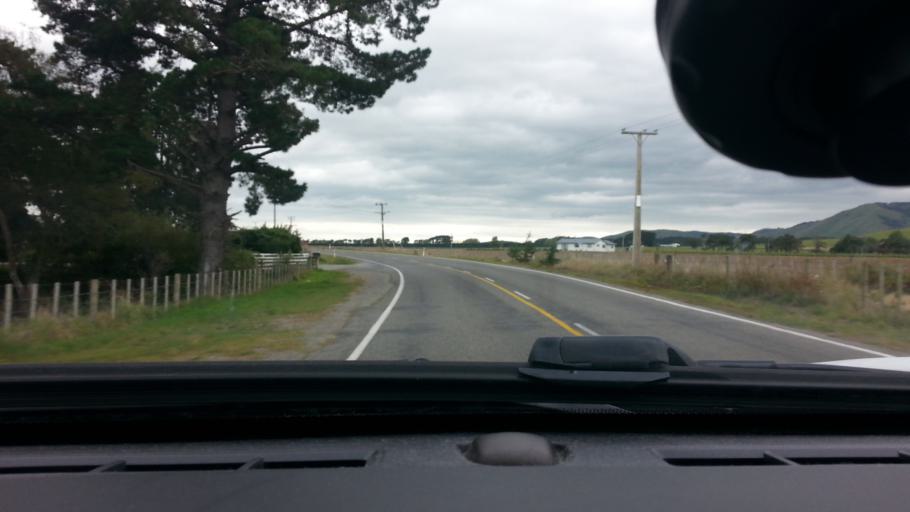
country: NZ
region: Wellington
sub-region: South Wairarapa District
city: Waipawa
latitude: -41.3125
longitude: 175.2644
